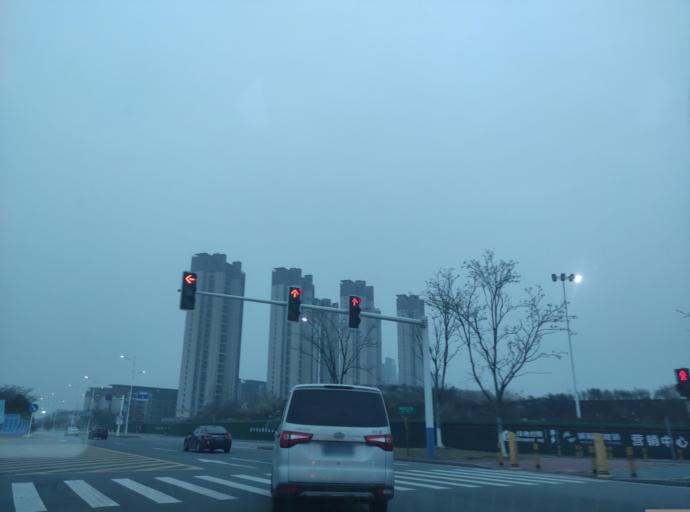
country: CN
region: Jiangxi Sheng
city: Pingxiang
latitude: 27.6717
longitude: 113.8526
